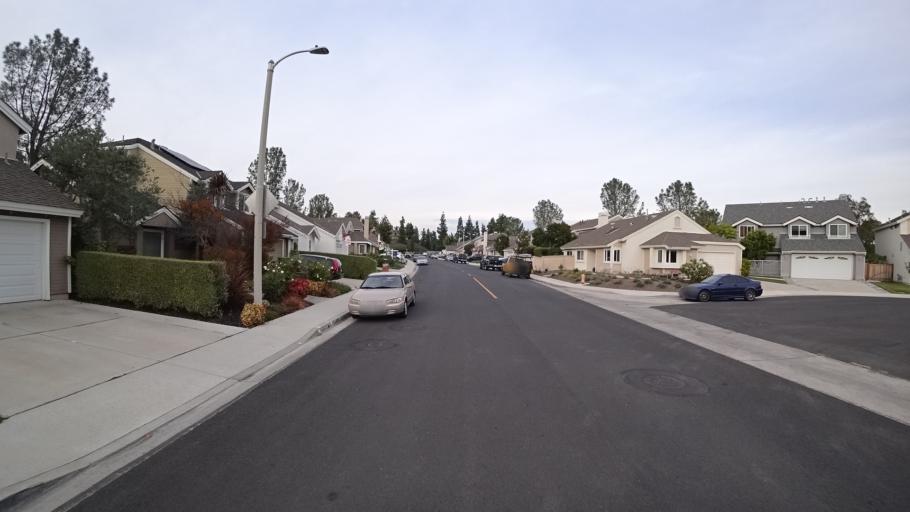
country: US
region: California
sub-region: Orange County
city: Laguna Woods
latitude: 33.5937
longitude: -117.7167
